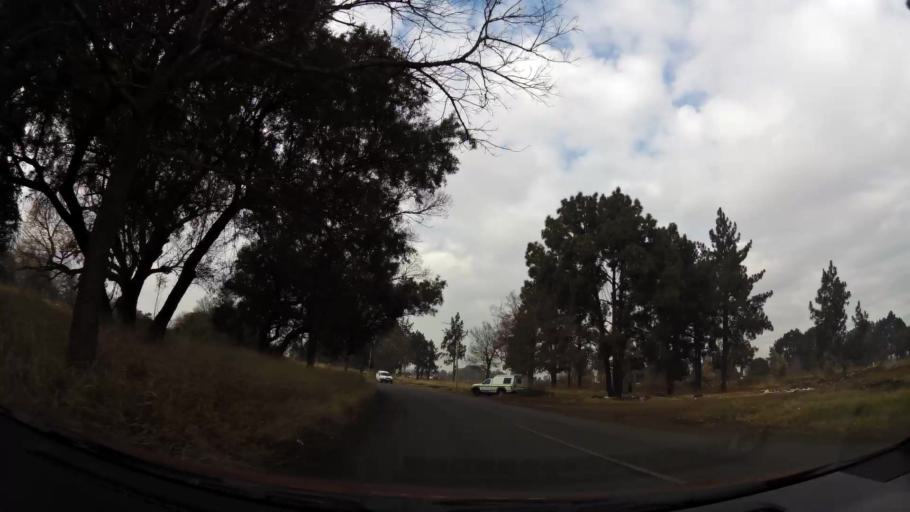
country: ZA
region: Gauteng
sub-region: Sedibeng District Municipality
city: Vanderbijlpark
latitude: -26.6948
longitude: 27.8112
